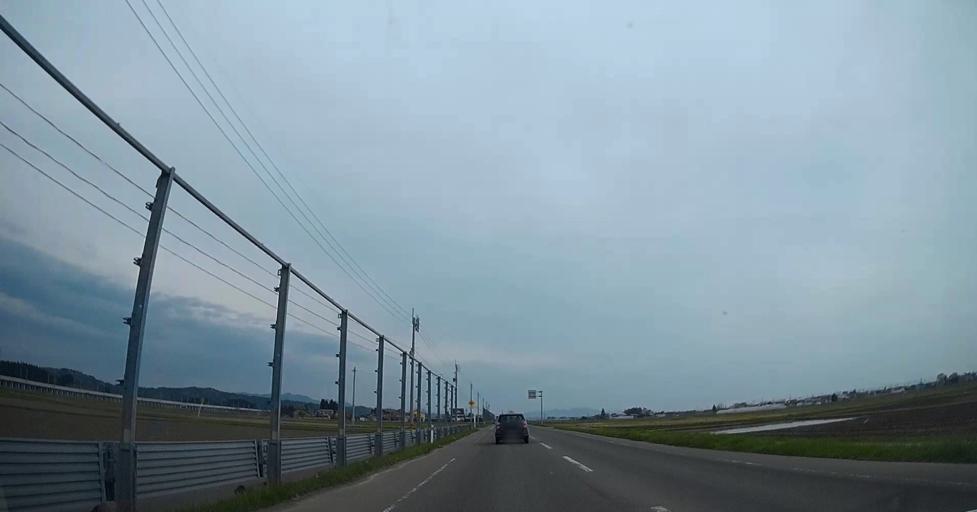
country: JP
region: Aomori
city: Aomori Shi
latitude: 40.8642
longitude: 140.6799
